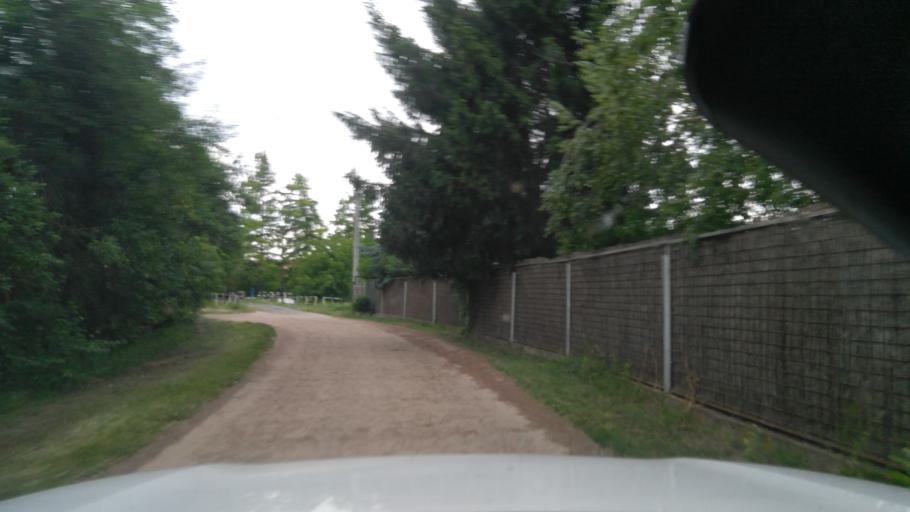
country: HU
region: Bekes
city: Bekescsaba
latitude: 46.6735
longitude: 21.1771
